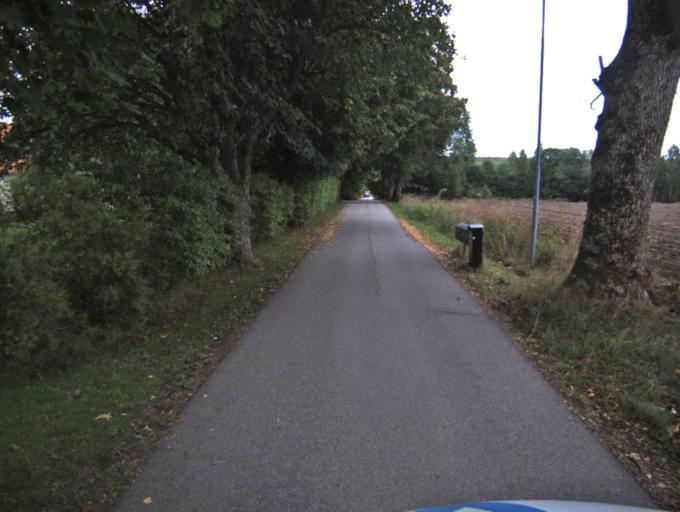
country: SE
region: Vaestra Goetaland
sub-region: Ulricehamns Kommun
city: Ulricehamn
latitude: 57.8403
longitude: 13.2927
